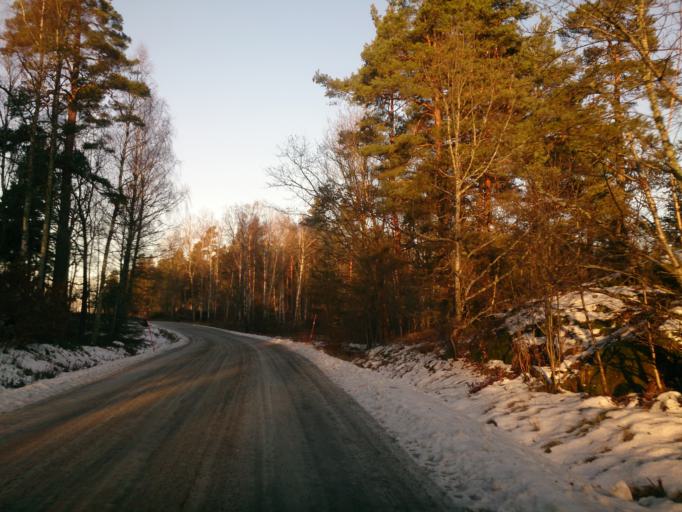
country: SE
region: OEstergoetland
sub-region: Linkopings Kommun
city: Sturefors
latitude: 58.2946
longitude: 15.8774
